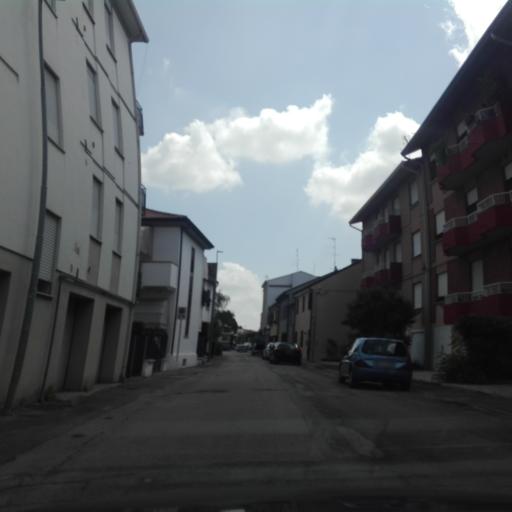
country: IT
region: Veneto
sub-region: Provincia di Rovigo
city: Rovigo
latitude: 45.0743
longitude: 11.7916
